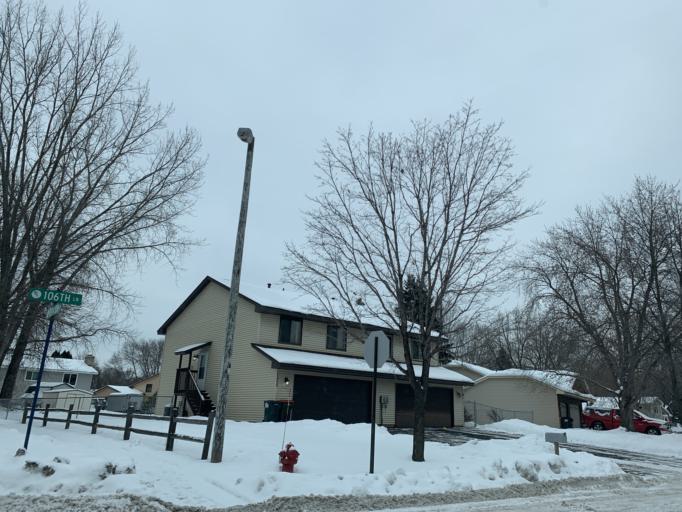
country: US
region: Minnesota
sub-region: Anoka County
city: Coon Rapids
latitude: 45.1640
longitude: -93.2995
